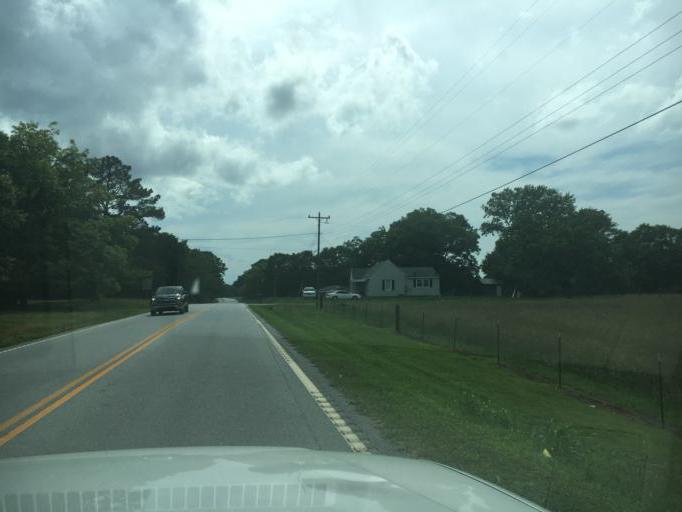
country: US
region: South Carolina
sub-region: Laurens County
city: Watts Mills
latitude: 34.5288
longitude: -81.9814
